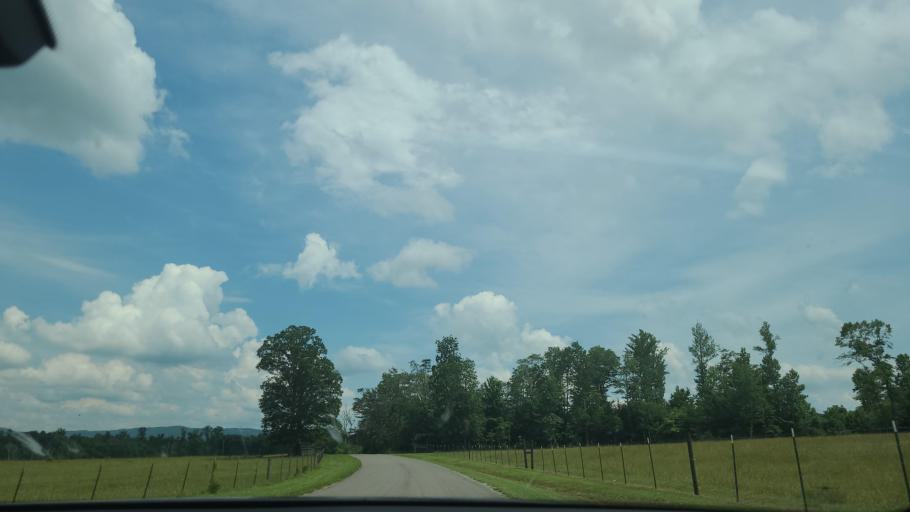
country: US
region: Tennessee
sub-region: Cumberland County
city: Lake Tansi
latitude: 35.7729
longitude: -85.0602
